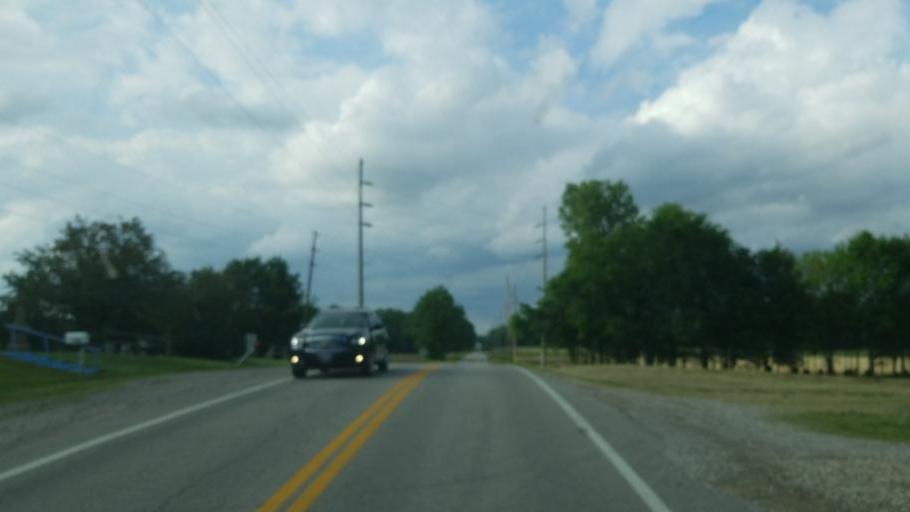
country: US
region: Ohio
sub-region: Delaware County
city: Sunbury
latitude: 40.2890
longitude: -82.7855
